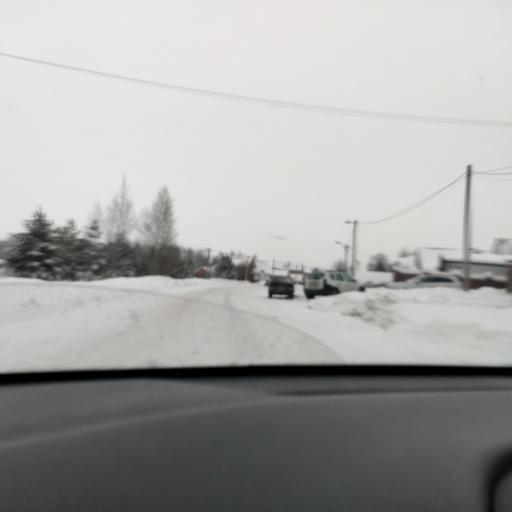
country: RU
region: Tatarstan
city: Vysokaya Gora
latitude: 55.9660
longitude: 49.1718
